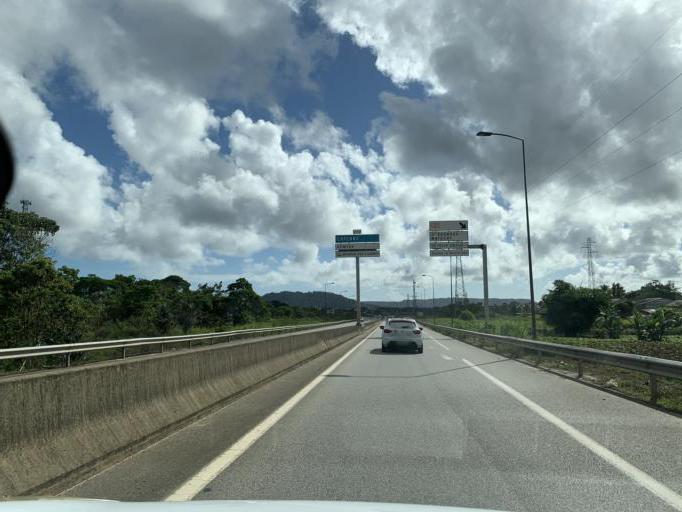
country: GF
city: Macouria
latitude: 4.8913
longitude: -52.3392
